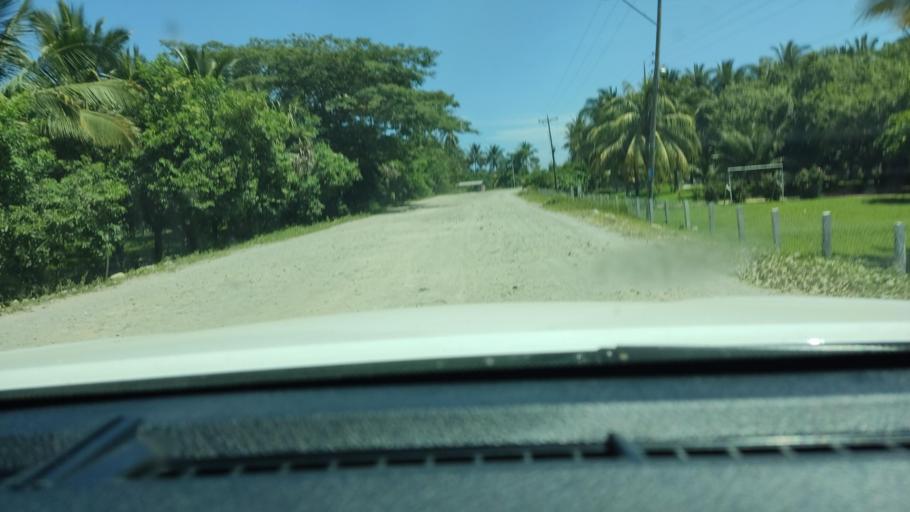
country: SV
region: Ahuachapan
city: San Francisco Menendez
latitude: 13.7646
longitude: -90.1159
